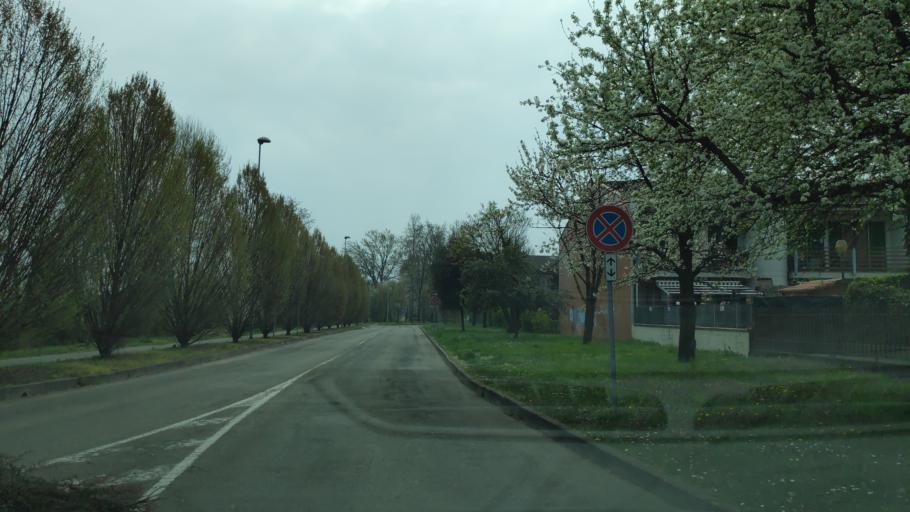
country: IT
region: Lombardy
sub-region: Citta metropolitana di Milano
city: Liscate
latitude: 45.4789
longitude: 9.4159
